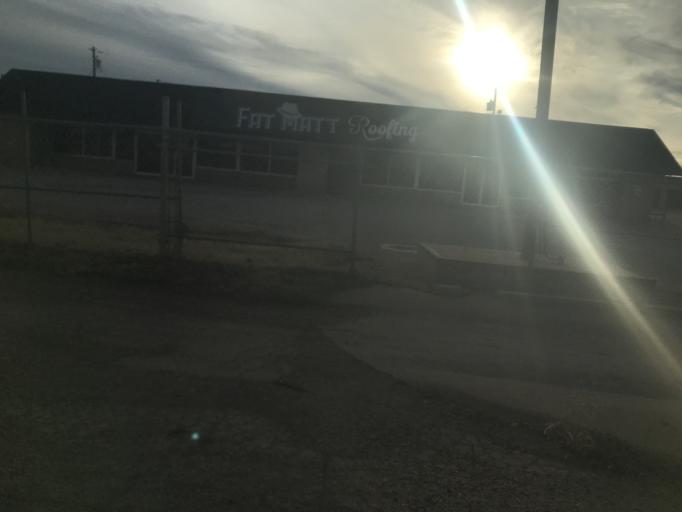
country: US
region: Texas
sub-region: Taylor County
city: Abilene
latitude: 32.4172
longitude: -99.7806
